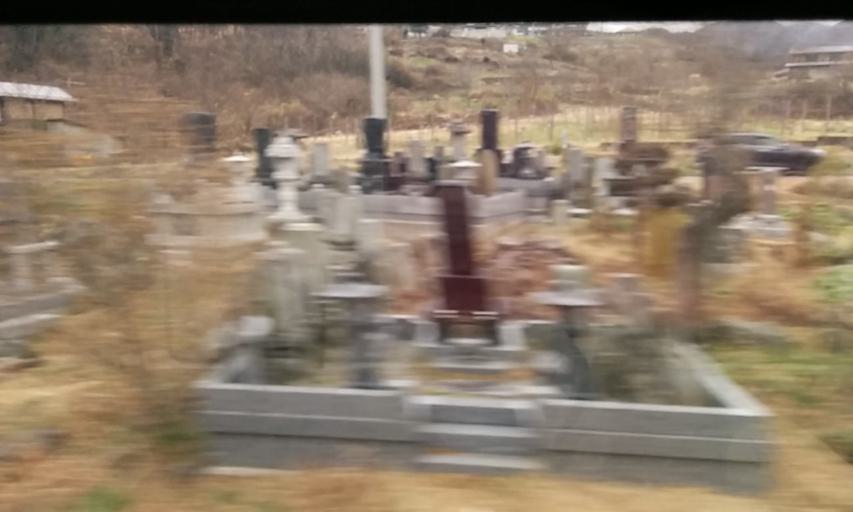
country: JP
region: Nagano
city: Omachi
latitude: 36.4505
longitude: 138.0400
